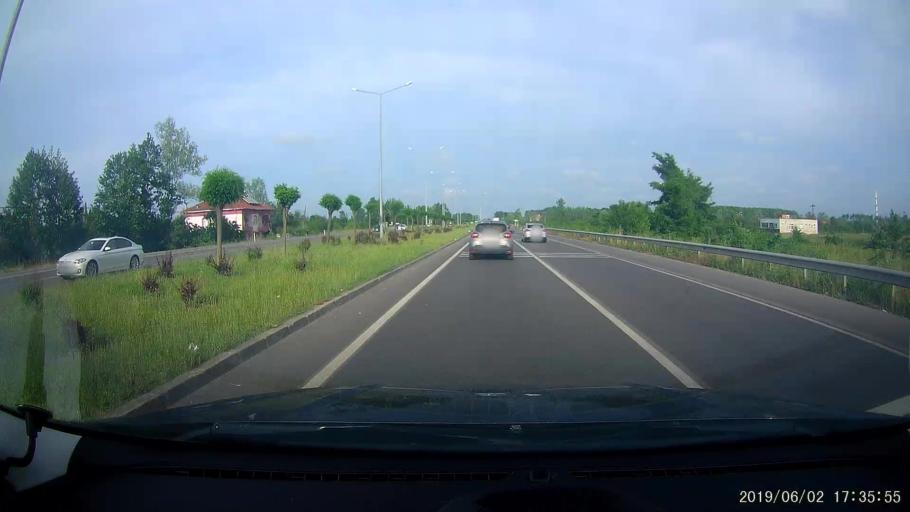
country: TR
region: Samsun
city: Terme
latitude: 41.2192
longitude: 36.8898
